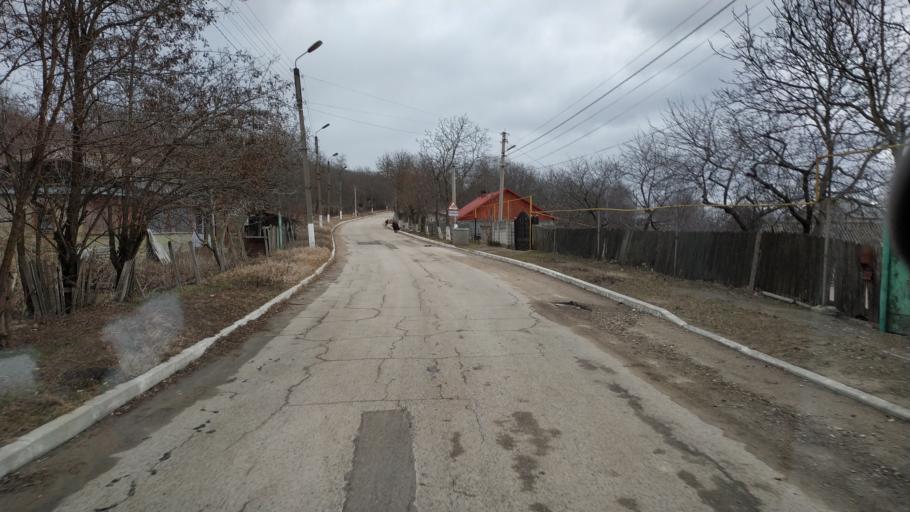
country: MD
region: Calarasi
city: Calarasi
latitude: 47.2659
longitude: 28.3523
